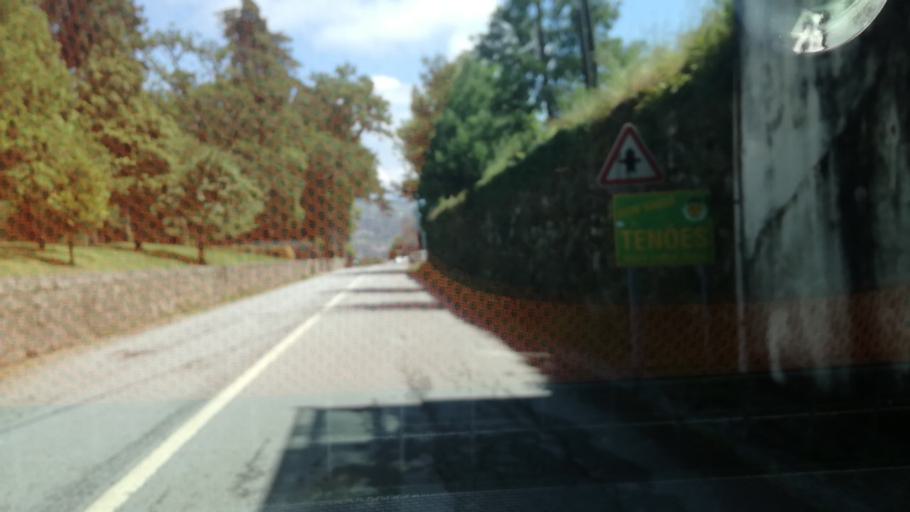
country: PT
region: Braga
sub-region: Braga
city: Adaufe
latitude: 41.5525
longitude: -8.3753
